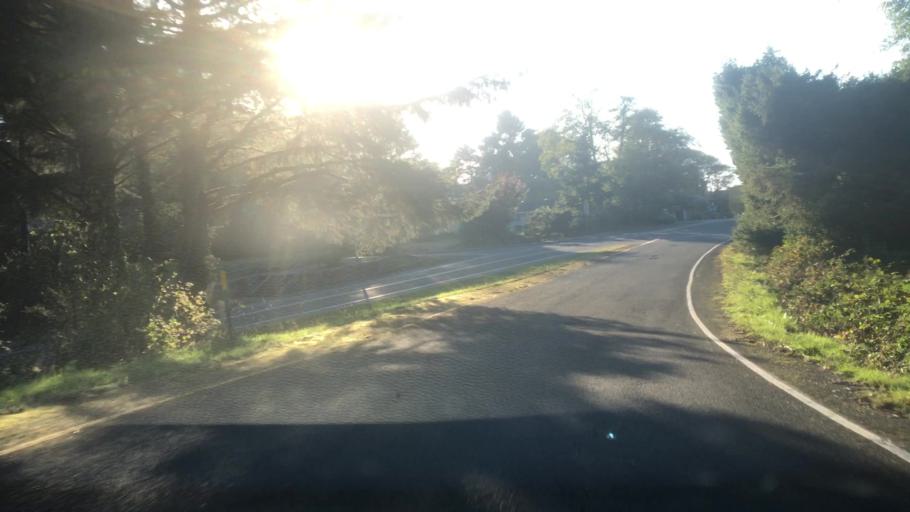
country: US
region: Oregon
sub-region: Clatsop County
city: Cannon Beach
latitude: 45.8880
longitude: -123.9584
